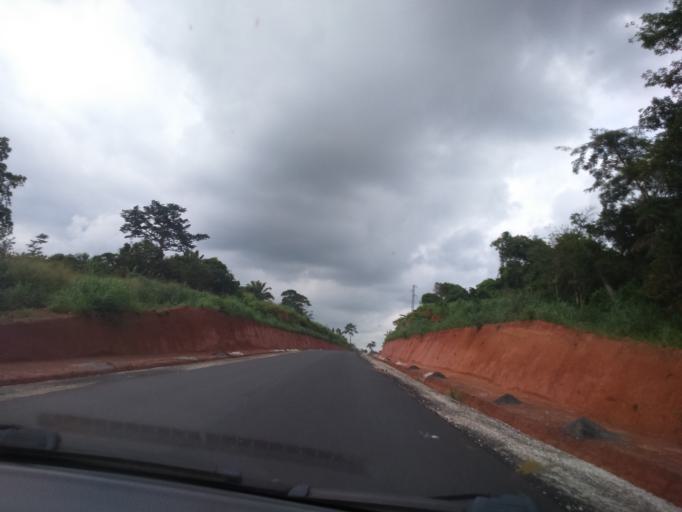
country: CI
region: Lagunes
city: Akoupe
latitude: 6.5022
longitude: -3.8247
